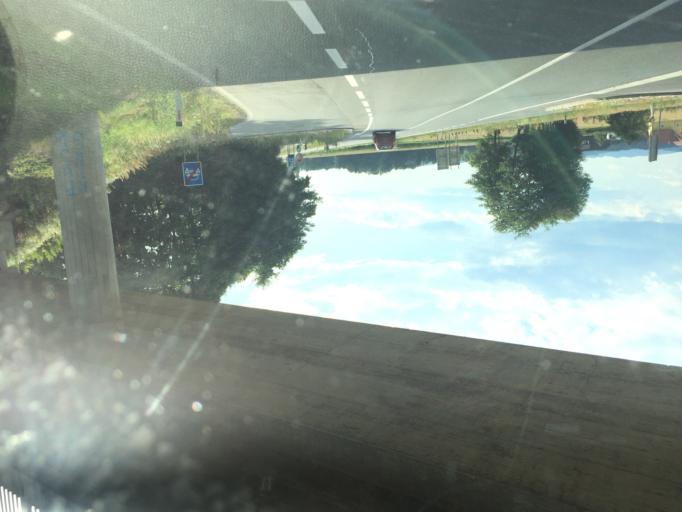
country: AT
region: Styria
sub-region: Politischer Bezirk Leibnitz
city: Sankt Veit am Vogau
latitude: 46.7482
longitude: 15.6217
